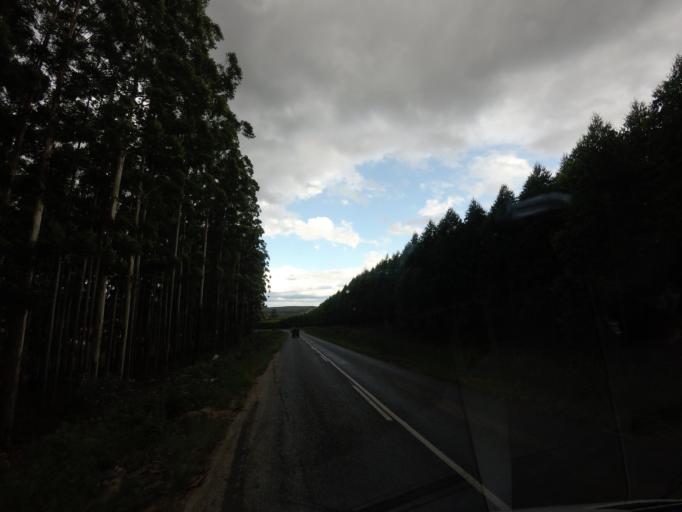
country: ZA
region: Mpumalanga
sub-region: Ehlanzeni District
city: Graksop
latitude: -24.9559
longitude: 30.9027
